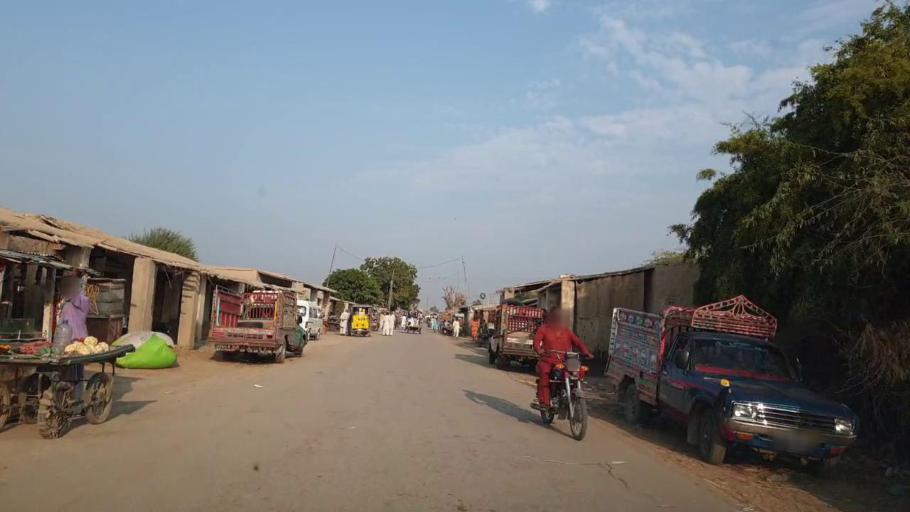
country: PK
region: Sindh
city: Pithoro
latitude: 25.5830
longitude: 69.3604
